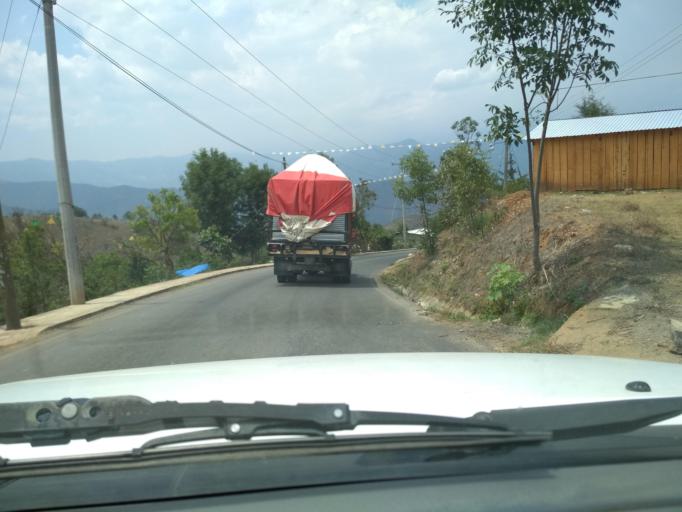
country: MX
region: Veracruz
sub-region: Acultzingo
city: Acatla
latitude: 18.7514
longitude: -97.1959
